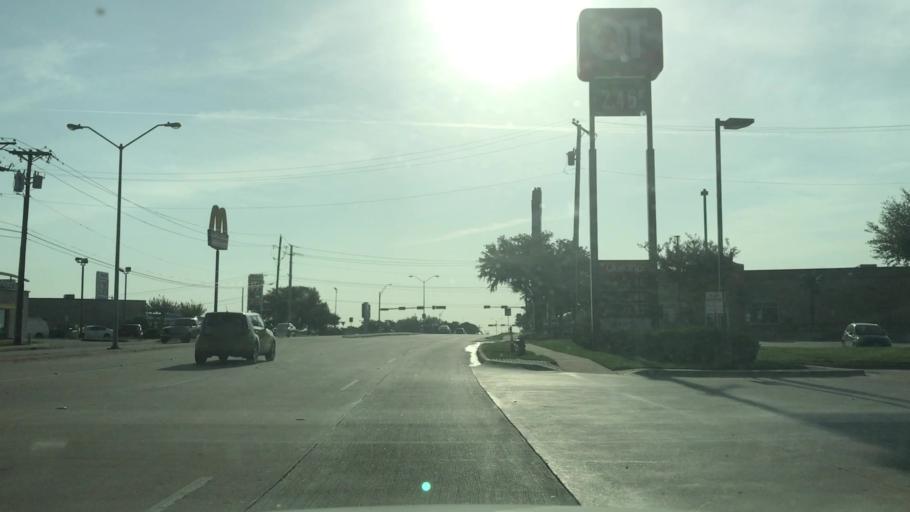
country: US
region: Texas
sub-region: Tarrant County
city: Euless
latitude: 32.7853
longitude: -97.0618
